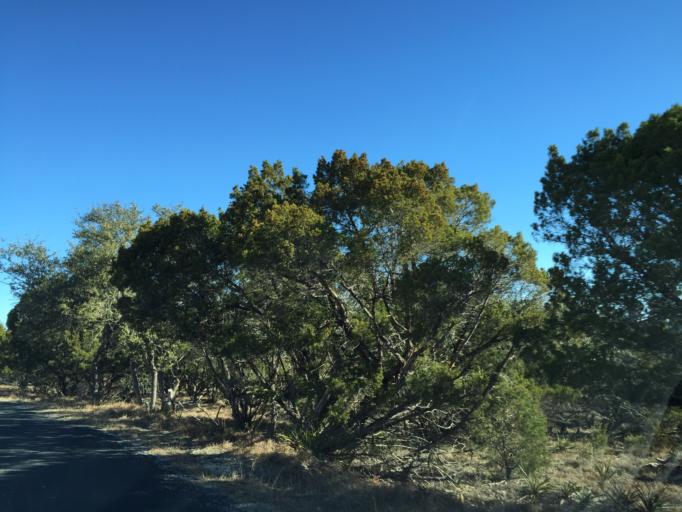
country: US
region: Texas
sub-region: Hays County
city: Woodcreek
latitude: 30.0096
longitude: -98.1148
